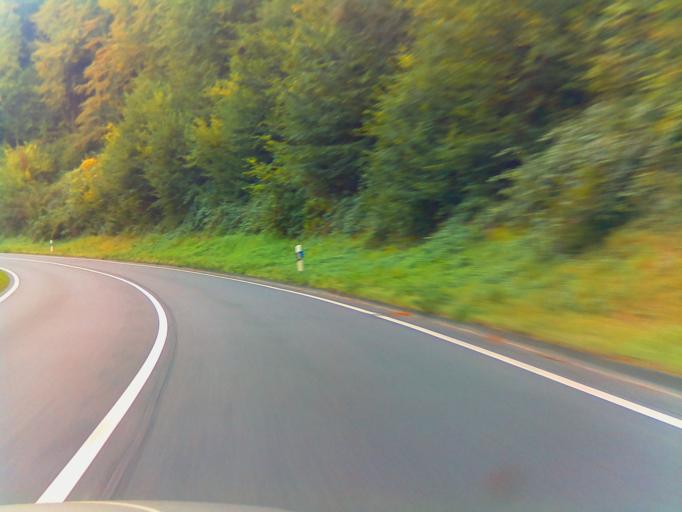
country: DE
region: Hesse
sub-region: Regierungsbezirk Darmstadt
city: Erbach
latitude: 49.6153
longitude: 8.9913
